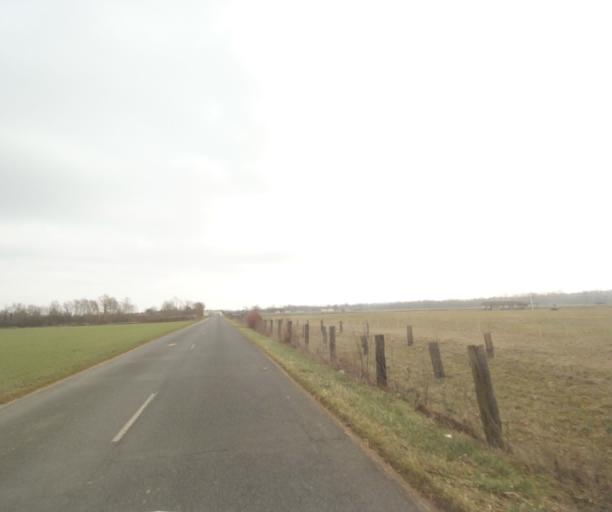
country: FR
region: Champagne-Ardenne
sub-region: Departement de la Haute-Marne
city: Villiers-en-Lieu
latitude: 48.6521
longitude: 4.8026
